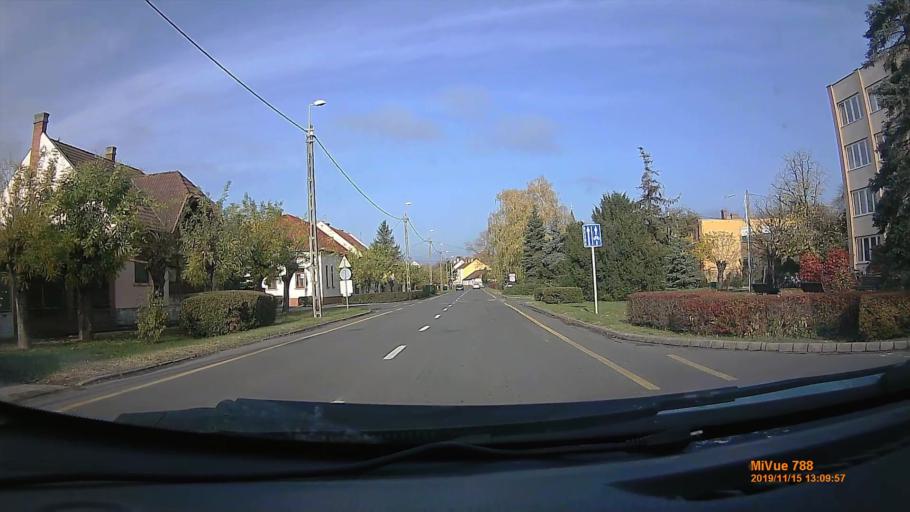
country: HU
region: Bekes
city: Gyula
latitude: 46.6414
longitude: 21.2792
